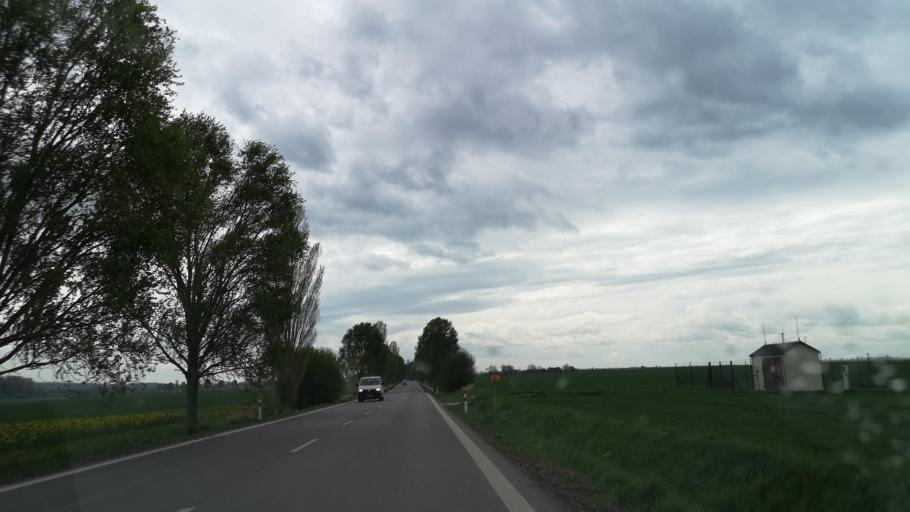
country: SK
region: Nitriansky
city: Zlate Moravce
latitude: 48.3268
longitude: 18.3492
